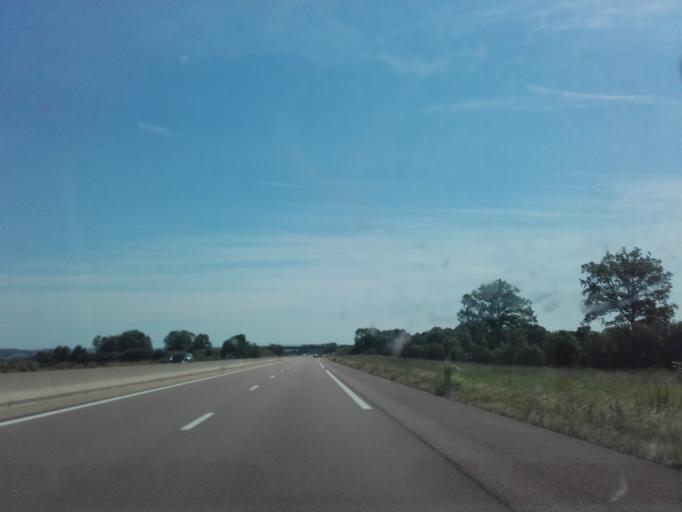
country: FR
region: Bourgogne
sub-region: Departement de l'Yonne
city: Avallon
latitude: 47.5045
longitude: 4.0490
